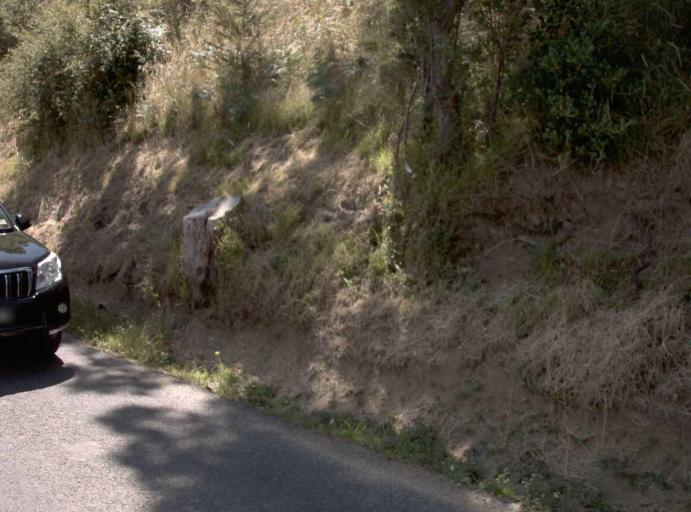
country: AU
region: Victoria
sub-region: Baw Baw
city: Warragul
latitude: -38.3473
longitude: 145.8987
